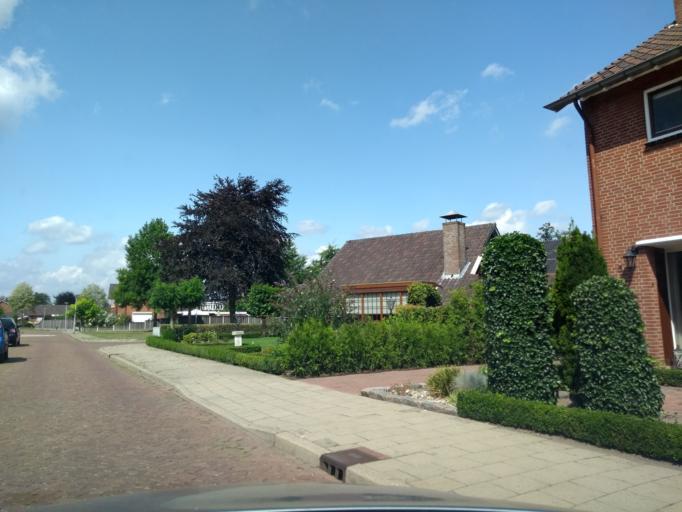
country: DE
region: Lower Saxony
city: Nordhorn
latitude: 52.3756
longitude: 7.0157
